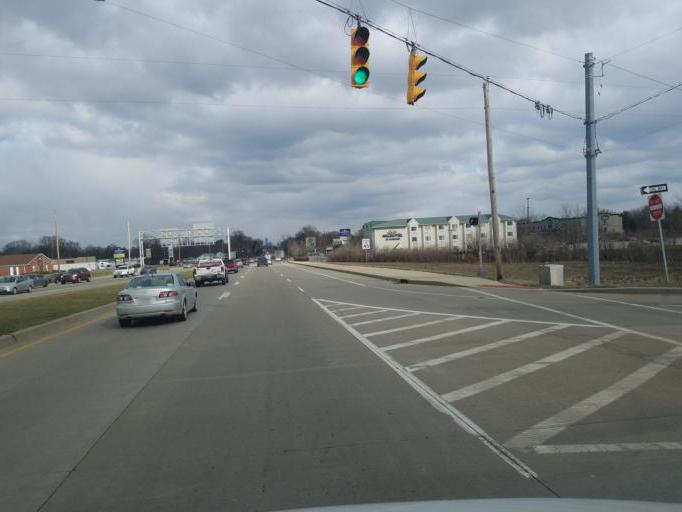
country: US
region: Indiana
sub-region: Marion County
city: Speedway
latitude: 39.7648
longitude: -86.2644
